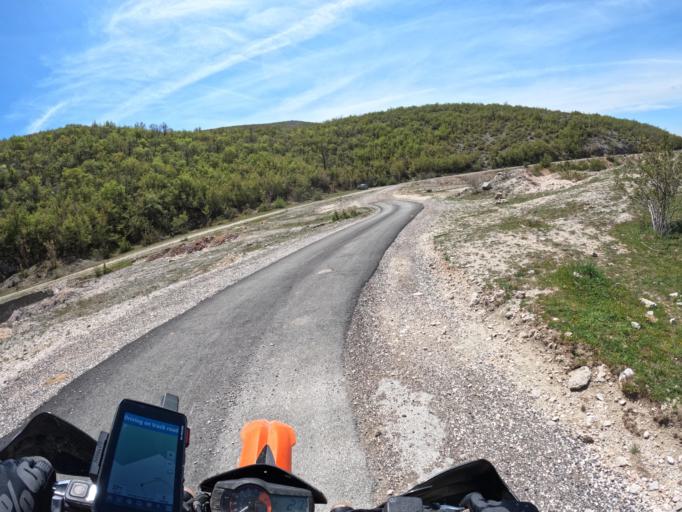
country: HR
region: Splitsko-Dalmatinska
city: Otok
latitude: 43.7012
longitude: 16.8106
